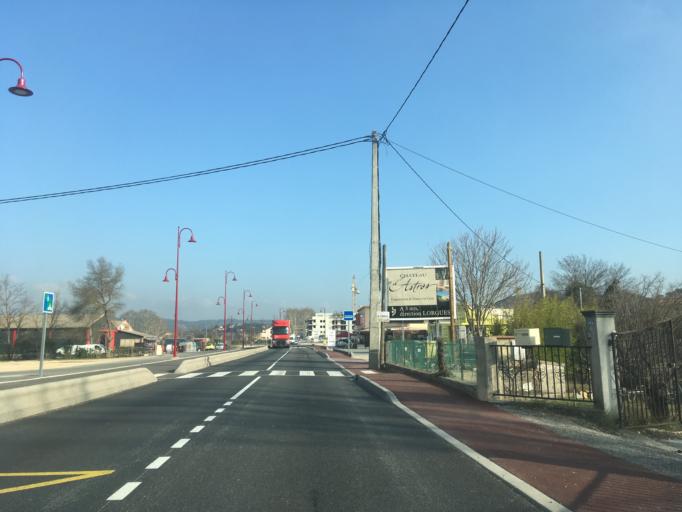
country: FR
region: Provence-Alpes-Cote d'Azur
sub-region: Departement du Var
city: Vidauban
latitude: 43.4210
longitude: 6.4253
